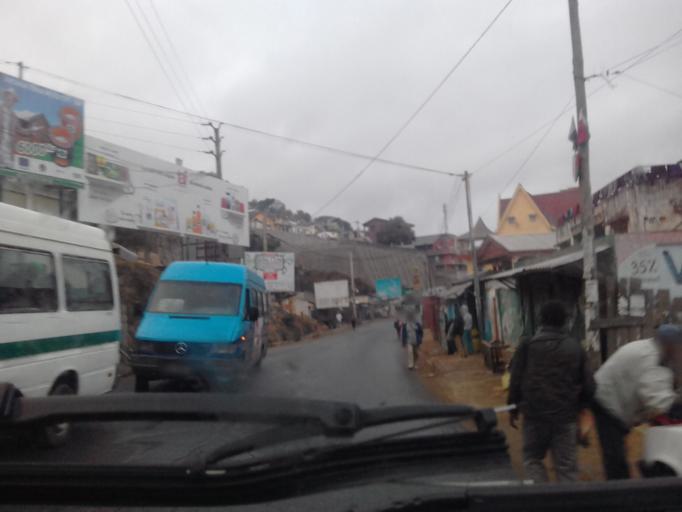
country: MG
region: Analamanga
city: Antananarivo
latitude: -18.8699
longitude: 47.5518
